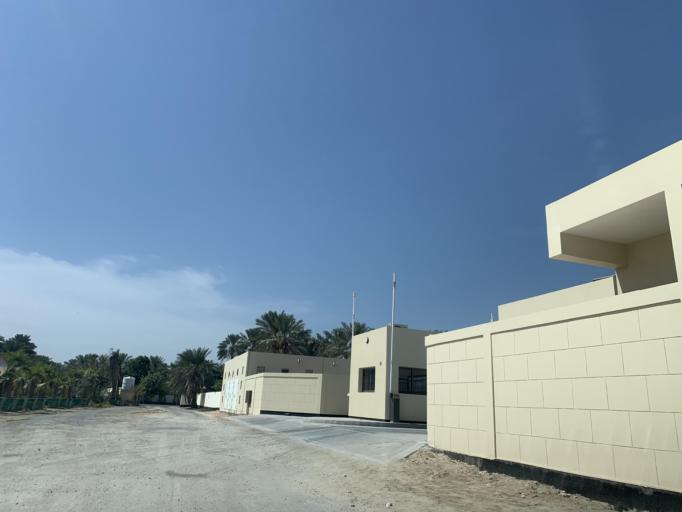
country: BH
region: Central Governorate
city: Madinat Hamad
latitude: 26.1843
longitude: 50.4687
